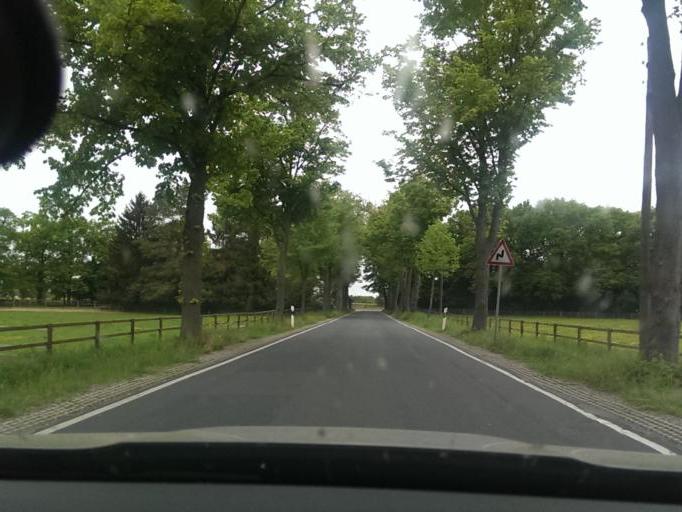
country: DE
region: Lower Saxony
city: Langenhagen
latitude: 52.4623
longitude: 9.7136
